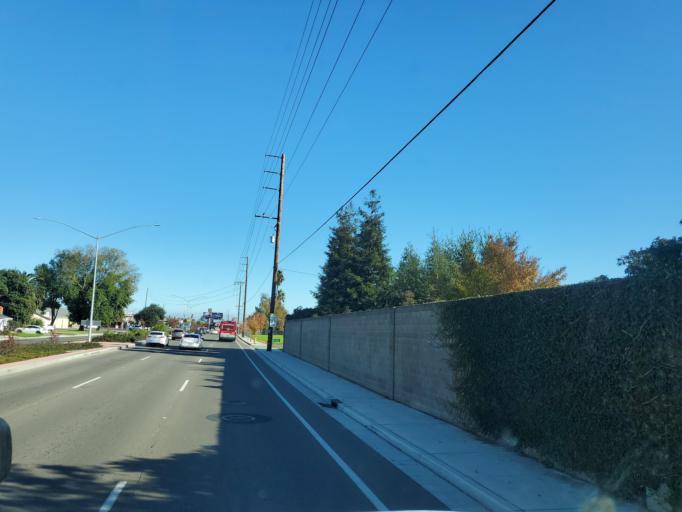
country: US
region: California
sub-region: San Joaquin County
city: Lincoln Village
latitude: 38.0209
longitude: -121.3287
